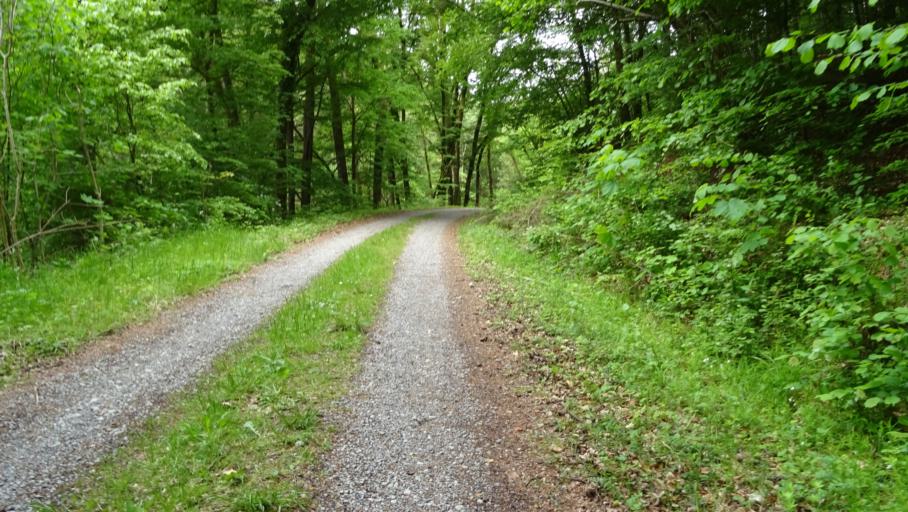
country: DE
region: Baden-Wuerttemberg
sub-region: Karlsruhe Region
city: Neckargerach
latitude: 49.4190
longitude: 9.0961
